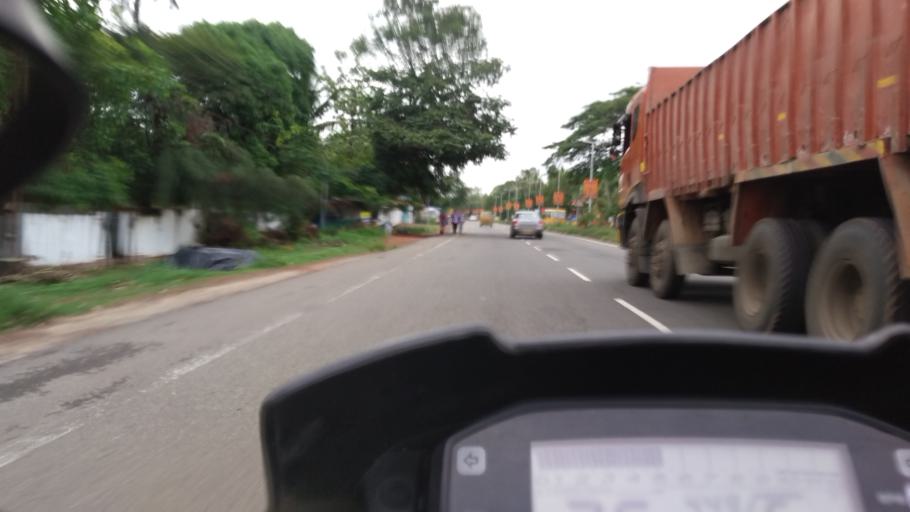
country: IN
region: Kerala
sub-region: Alappuzha
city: Kutiatodu
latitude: 9.8171
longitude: 76.3130
